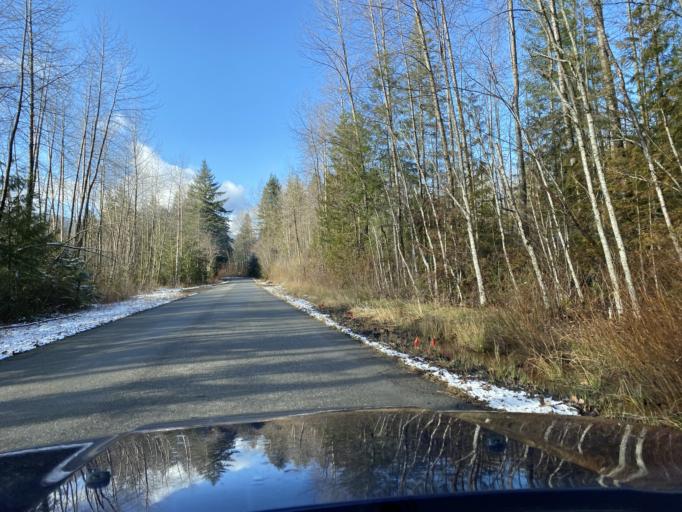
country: US
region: Washington
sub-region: King County
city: Snoqualmie
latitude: 47.5075
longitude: -121.8786
